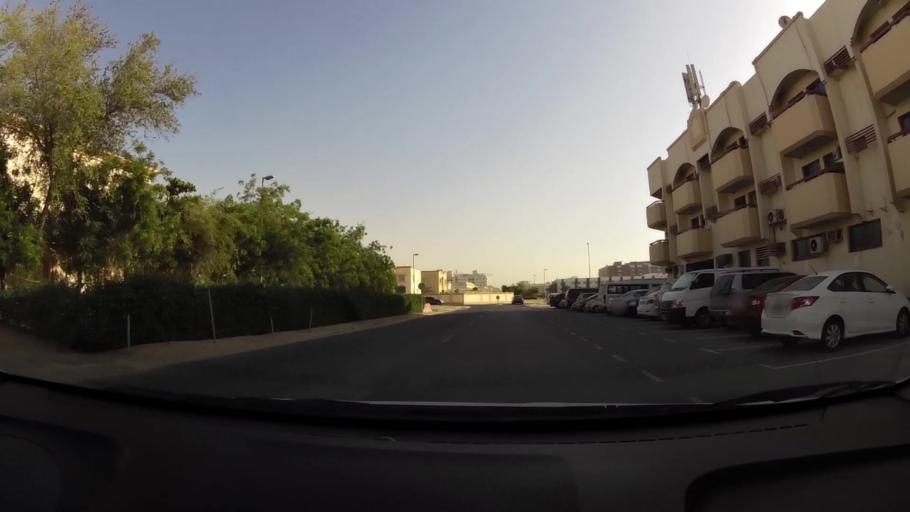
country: AE
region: Ash Shariqah
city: Sharjah
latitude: 25.2719
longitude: 55.3839
